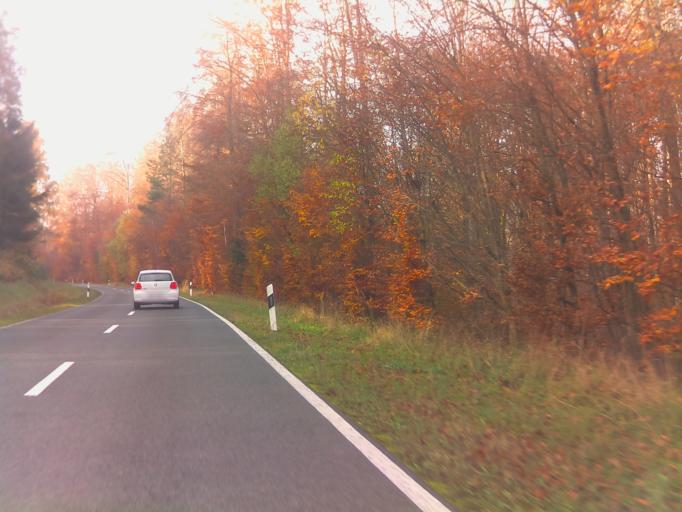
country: DE
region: Bavaria
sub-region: Regierungsbezirk Unterfranken
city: Schondra
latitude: 50.2465
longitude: 9.9149
